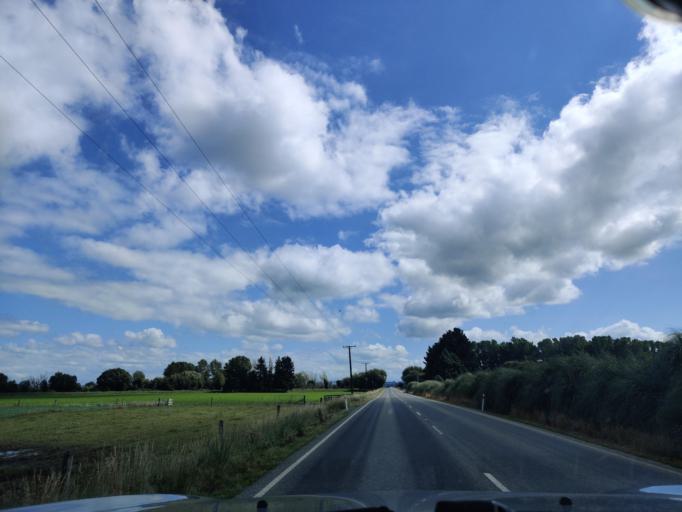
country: NZ
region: Canterbury
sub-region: Timaru District
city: Pleasant Point
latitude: -44.1264
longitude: 171.2618
